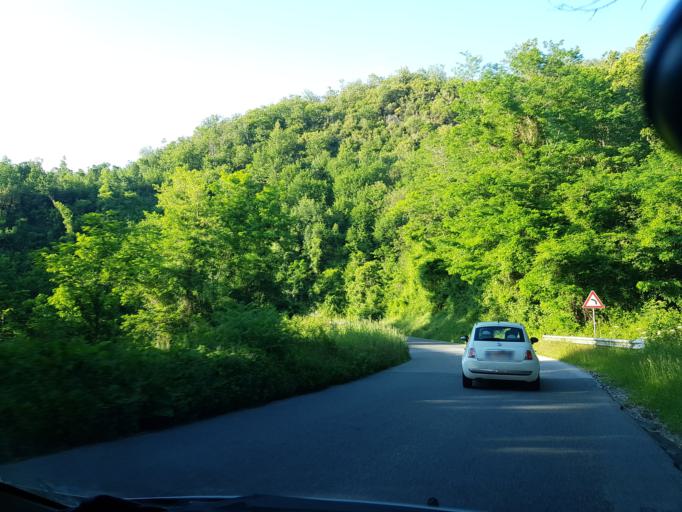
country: IT
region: Tuscany
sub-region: Provincia di Lucca
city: Minucciano
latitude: 44.1798
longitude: 10.2026
